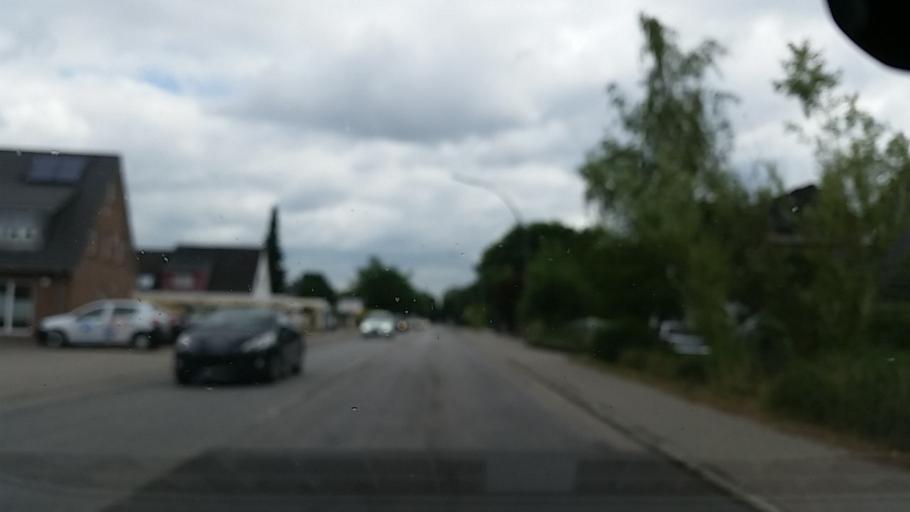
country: DE
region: Schleswig-Holstein
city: Tangstedt
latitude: 53.7048
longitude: 10.0623
